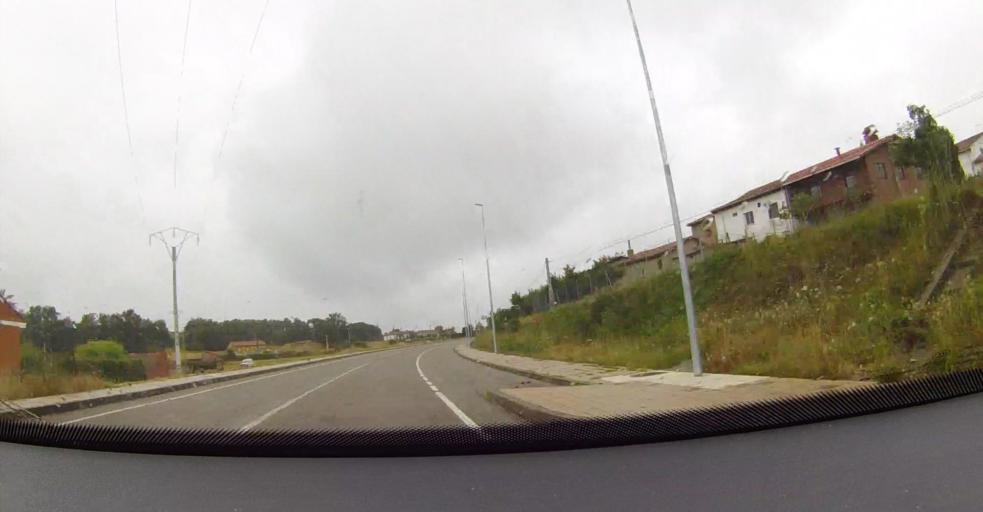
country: ES
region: Castille and Leon
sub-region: Provincia de Leon
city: Bonar
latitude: 42.8403
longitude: -5.2514
